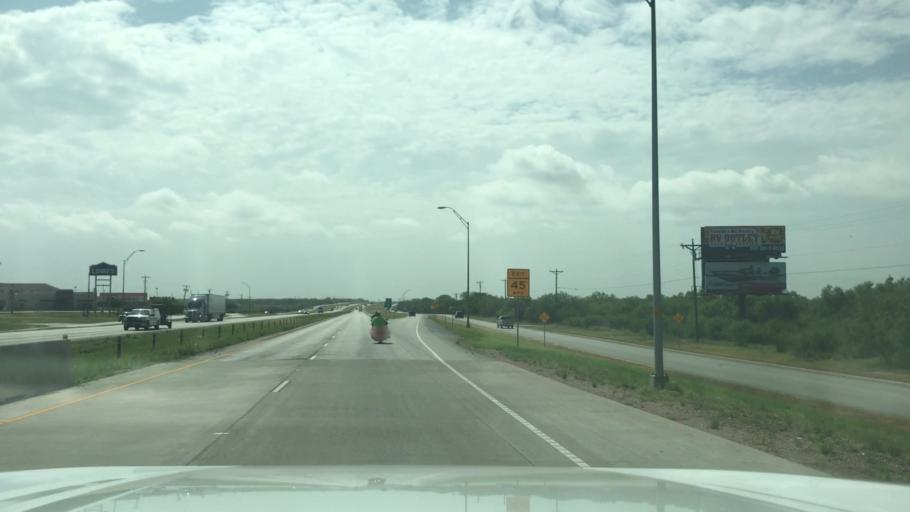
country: US
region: Texas
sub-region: Taylor County
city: Abilene
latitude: 32.4755
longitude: -99.6971
